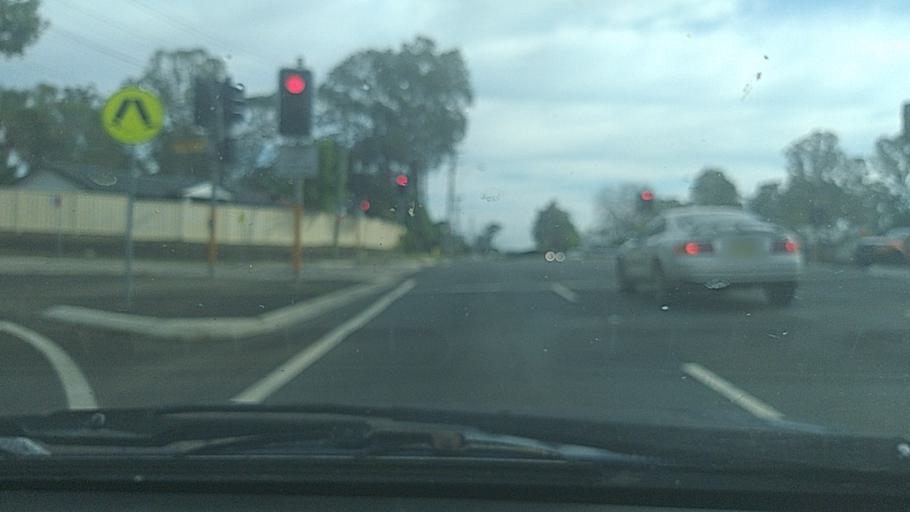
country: AU
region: New South Wales
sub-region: Penrith Municipality
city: Cambridge Park
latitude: -33.7473
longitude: 150.7142
